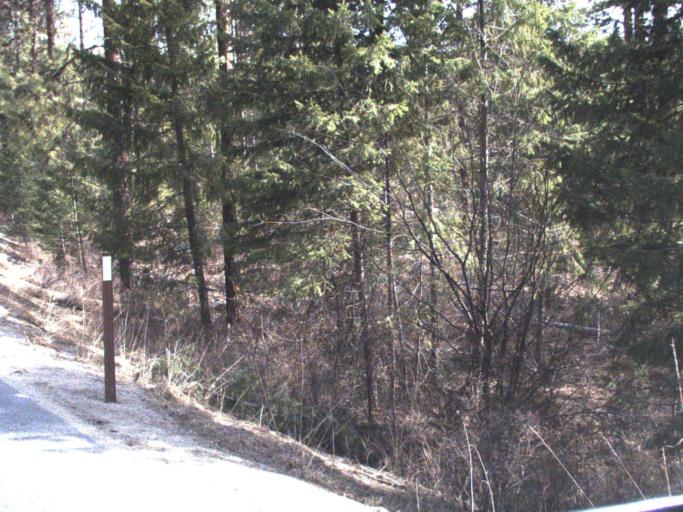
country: US
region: Washington
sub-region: Stevens County
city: Chewelah
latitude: 48.5090
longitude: -117.6637
